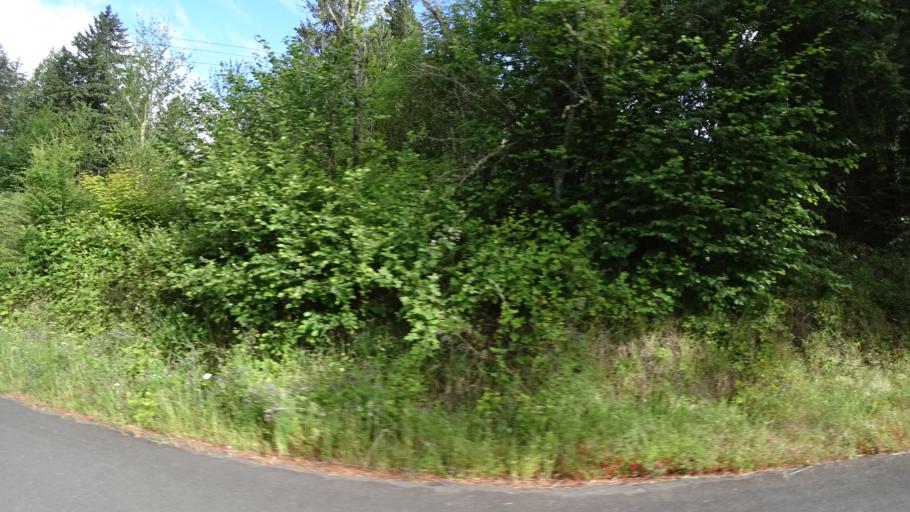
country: US
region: Oregon
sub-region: Washington County
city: Oak Hills
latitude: 45.5804
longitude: -122.8209
